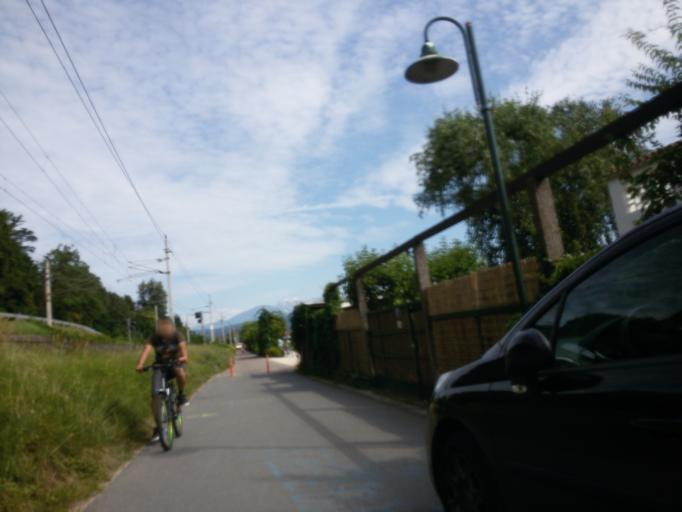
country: AT
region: Carinthia
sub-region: Klagenfurt am Woerthersee
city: Klagenfurt am Woerthersee
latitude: 46.6265
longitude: 14.2428
